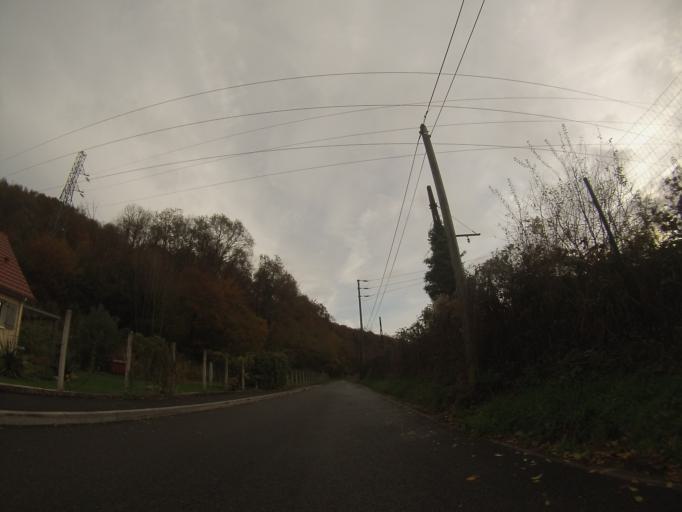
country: FR
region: Aquitaine
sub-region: Departement des Pyrenees-Atlantiques
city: Jurancon
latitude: 43.2740
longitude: -0.3857
